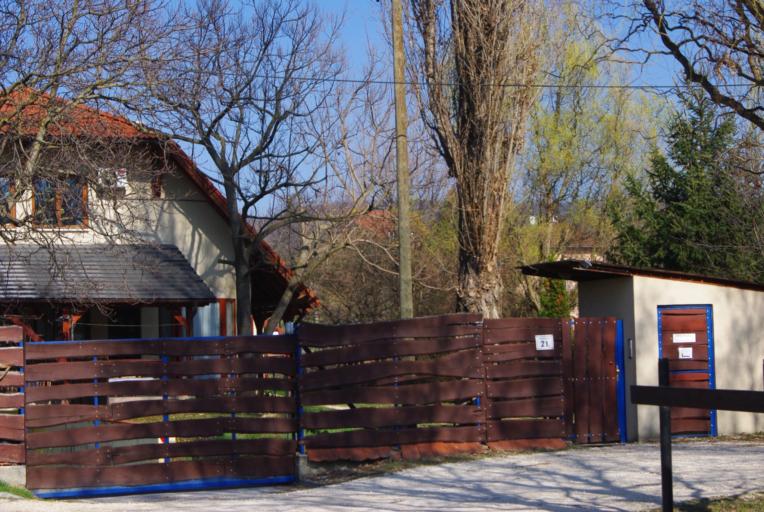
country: HU
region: Pest
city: Budakeszi
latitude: 47.5042
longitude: 18.9177
